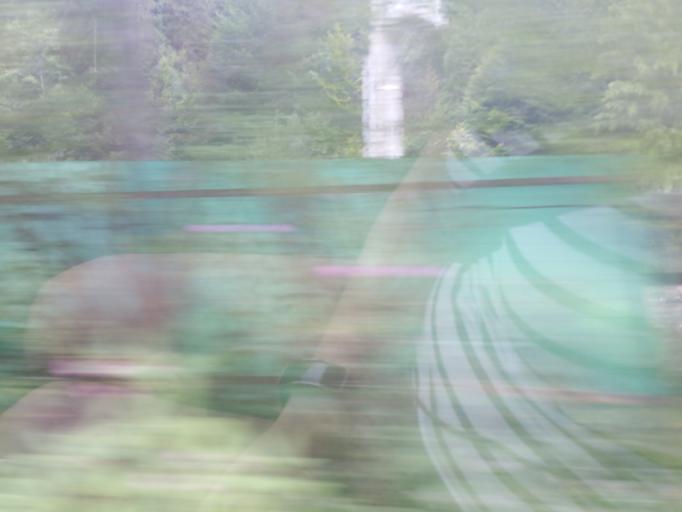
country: RO
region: Alba
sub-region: Comuna Garda de Sus
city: Garda de Sus
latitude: 46.4669
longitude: 22.8217
